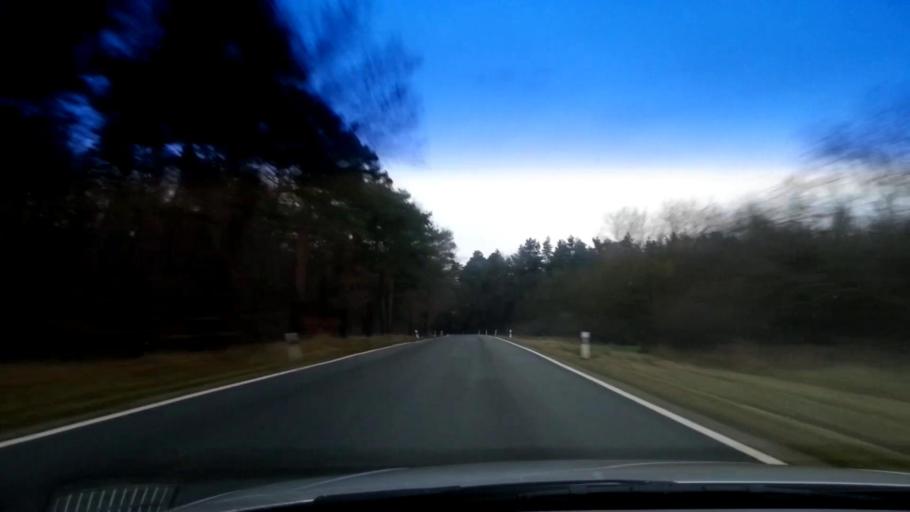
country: DE
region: Bavaria
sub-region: Regierungsbezirk Mittelfranken
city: Muhlhausen
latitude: 49.7954
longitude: 10.7855
